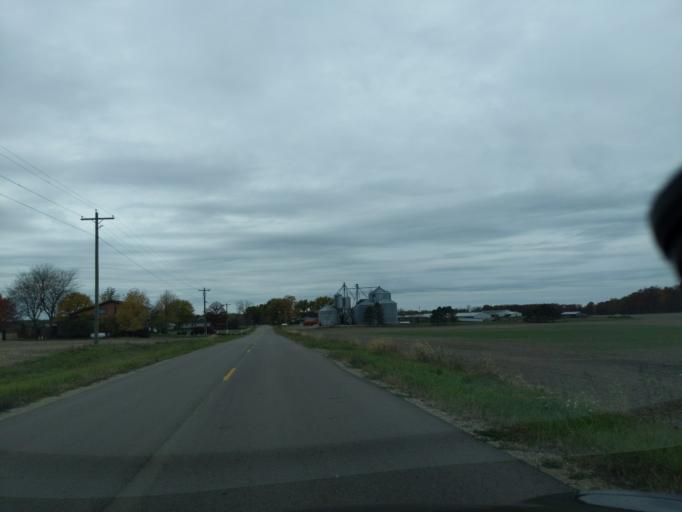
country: US
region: Michigan
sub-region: Eaton County
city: Eaton Rapids
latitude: 42.4365
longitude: -84.6033
